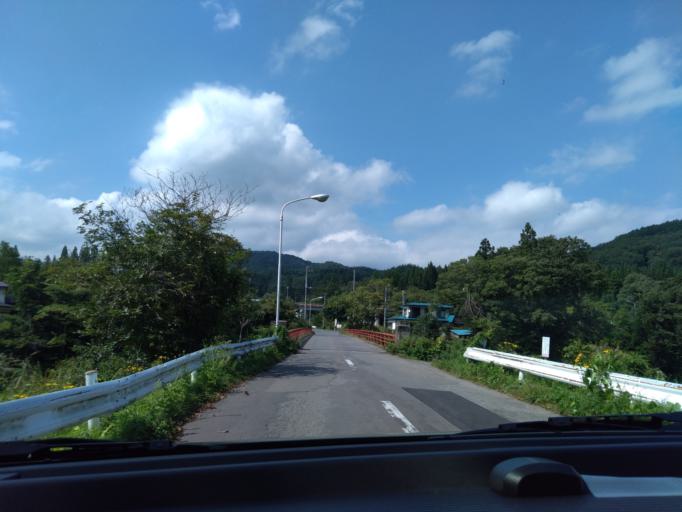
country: JP
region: Iwate
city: Shizukuishi
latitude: 39.6845
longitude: 140.9121
